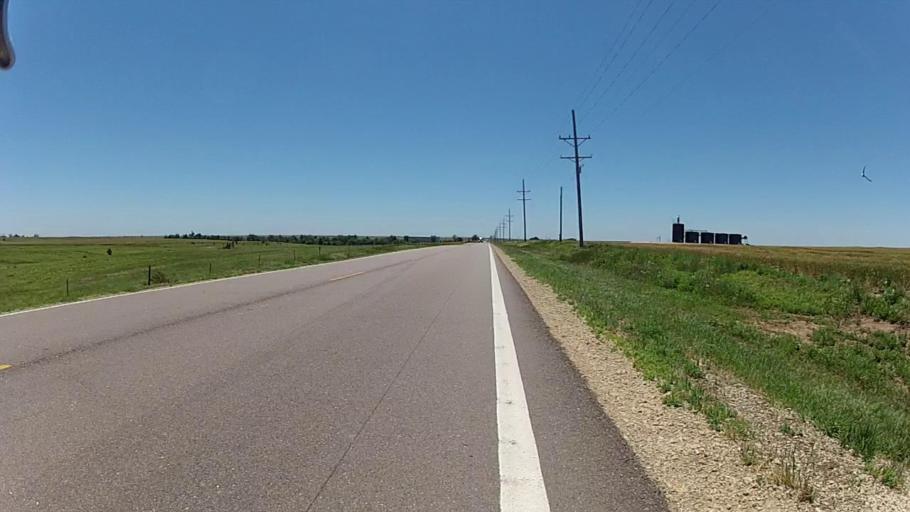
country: US
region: Kansas
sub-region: Kiowa County
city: Greensburg
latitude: 37.5100
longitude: -99.3204
